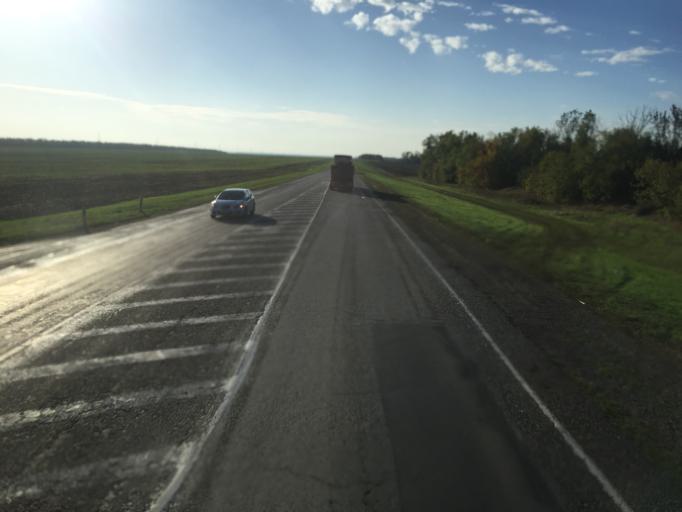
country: RU
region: Rostov
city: Mechetinskaya
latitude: 46.6979
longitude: 40.5073
